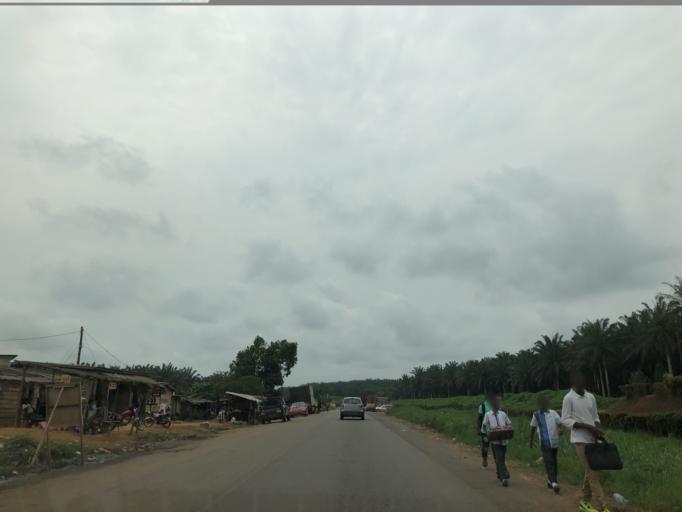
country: CM
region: Littoral
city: Edea
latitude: 3.5786
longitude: 10.1104
